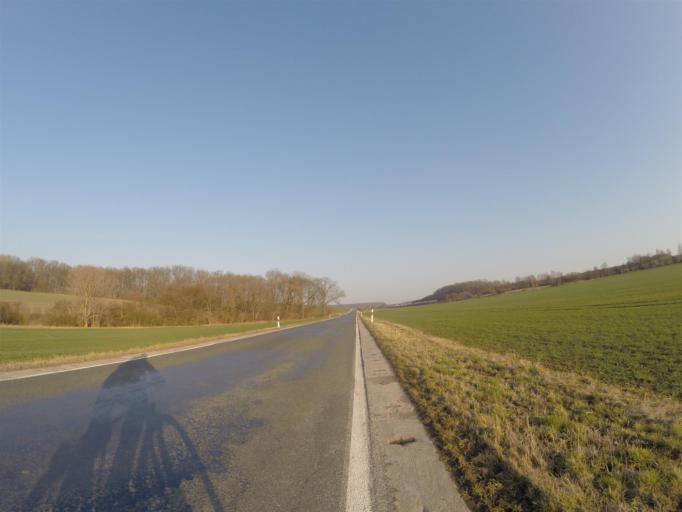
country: DE
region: Thuringia
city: Lehnstedt
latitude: 50.9380
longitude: 11.4460
